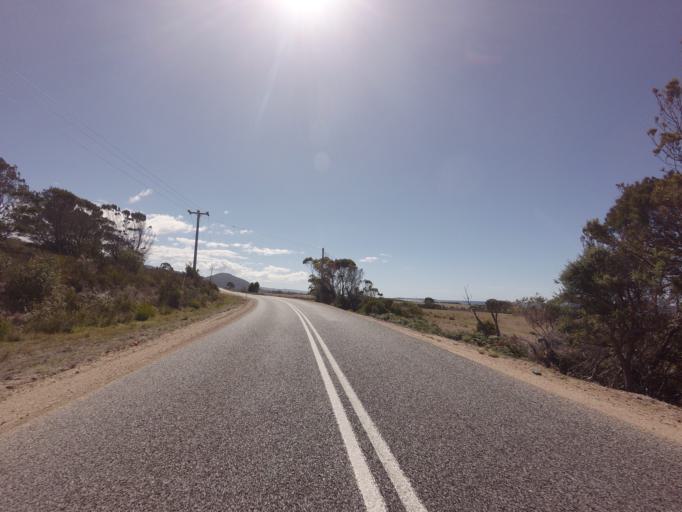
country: AU
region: Tasmania
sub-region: Break O'Day
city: St Helens
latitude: -41.7932
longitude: 148.2627
